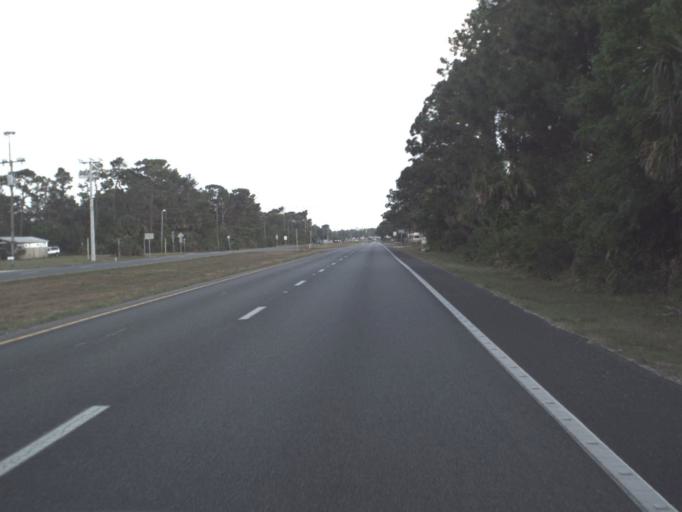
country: US
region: Florida
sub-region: Brevard County
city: Mims
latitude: 28.7020
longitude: -80.8602
